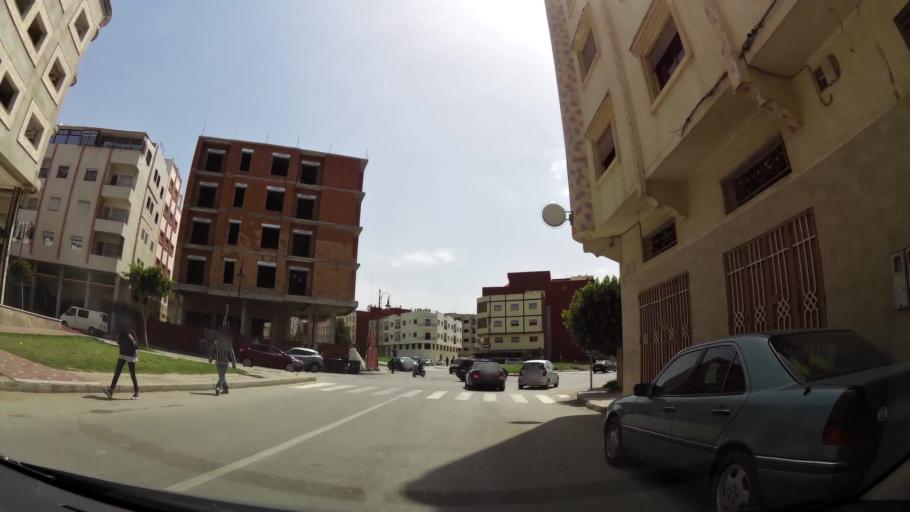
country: MA
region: Tanger-Tetouan
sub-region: Tanger-Assilah
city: Tangier
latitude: 35.7557
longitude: -5.8402
